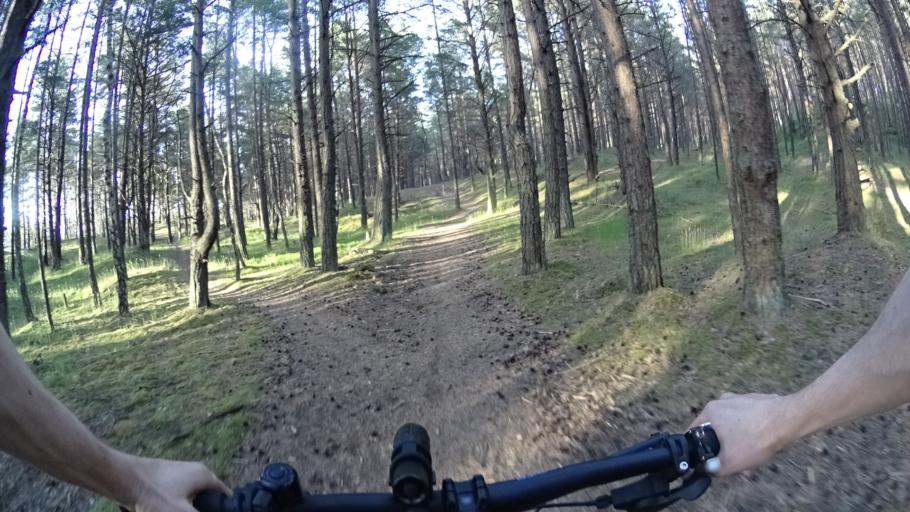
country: LV
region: Riga
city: Jaunciems
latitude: 57.1084
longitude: 24.1812
